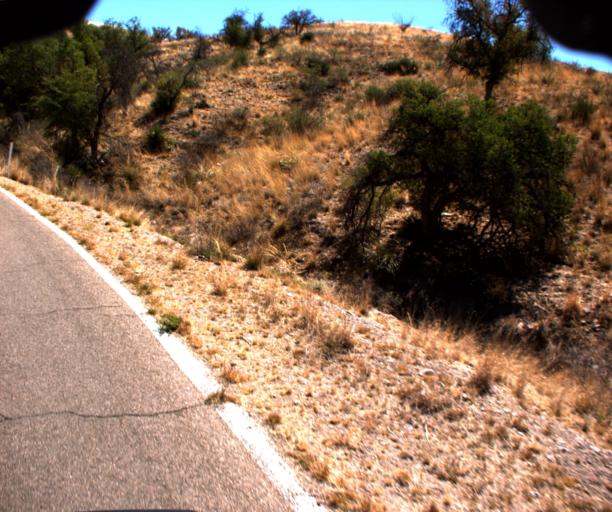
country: US
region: Arizona
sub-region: Santa Cruz County
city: Rio Rico
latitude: 31.3899
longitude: -111.0732
